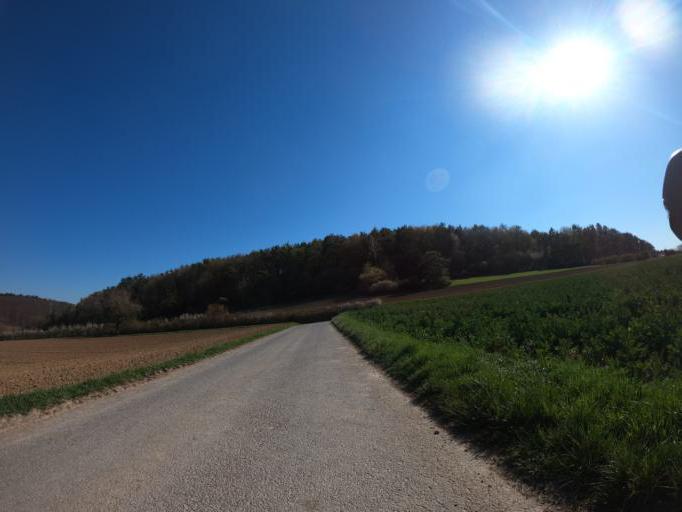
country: DE
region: Baden-Wuerttemberg
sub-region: Karlsruhe Region
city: Monsheim
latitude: 48.8698
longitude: 8.8606
